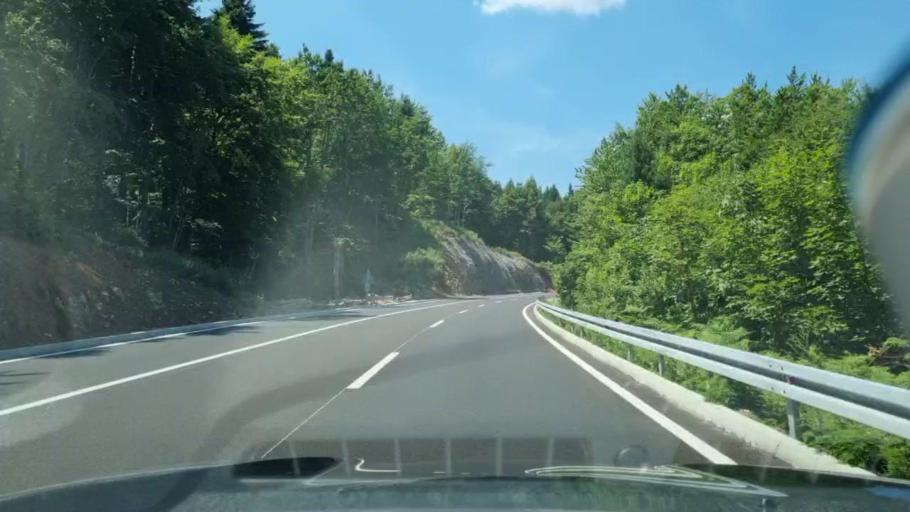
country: BA
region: Federation of Bosnia and Herzegovina
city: Velagici
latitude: 44.5486
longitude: 16.6783
